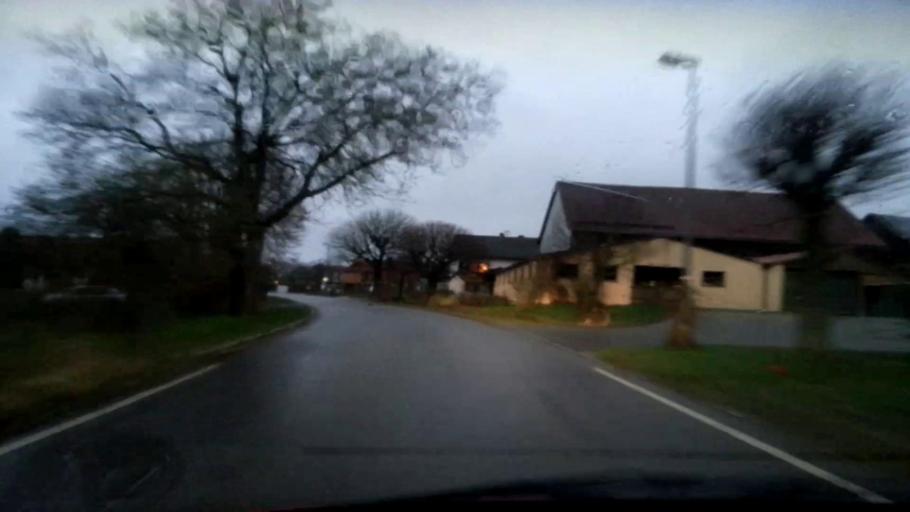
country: DE
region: Bavaria
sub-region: Upper Franconia
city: Poxdorf
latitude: 49.9698
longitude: 11.1287
